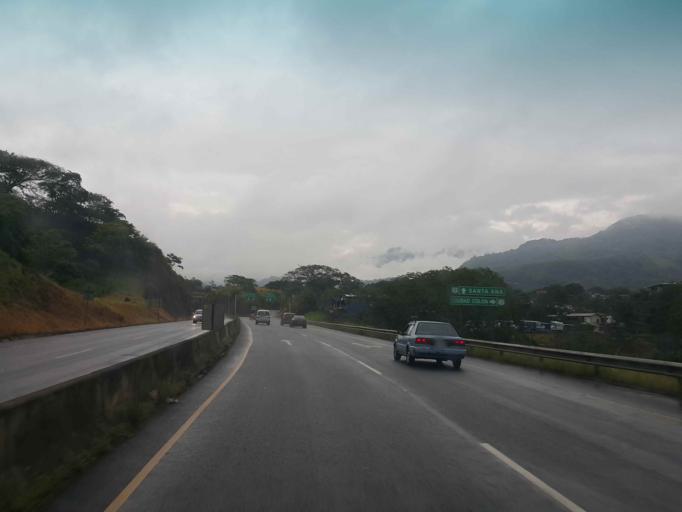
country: CR
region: Heredia
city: Colon
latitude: 9.9383
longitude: -84.2240
